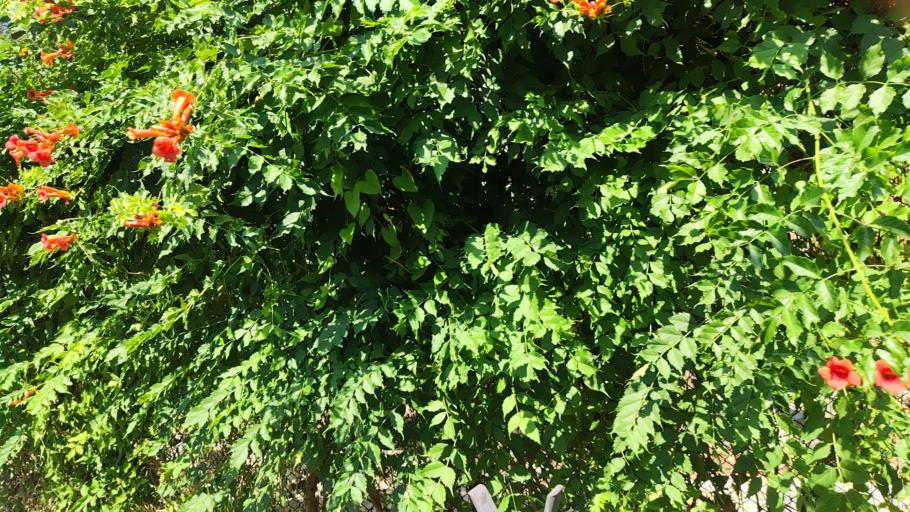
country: TR
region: Mugla
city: Sarigerme
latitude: 36.7029
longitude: 28.6952
